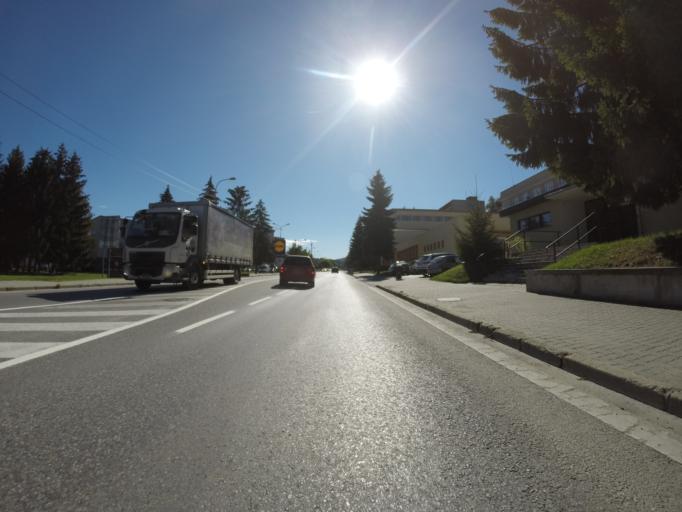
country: SK
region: Trenciansky
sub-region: Okres Povazska Bystrica
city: Povazska Bystrica
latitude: 49.1154
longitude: 18.4432
